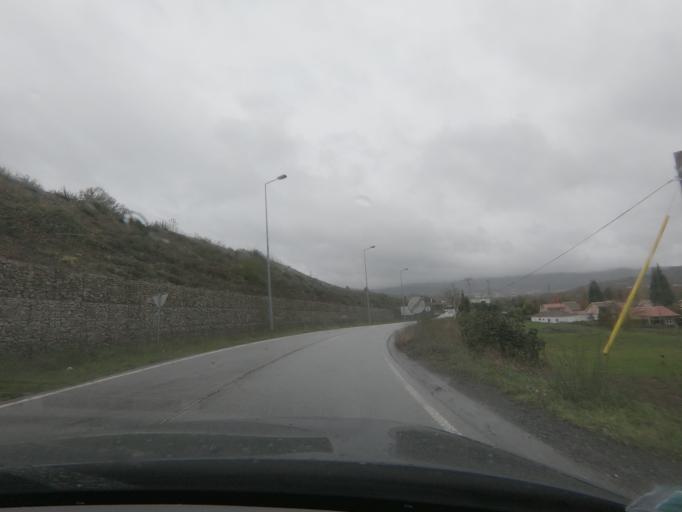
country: PT
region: Vila Real
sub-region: Santa Marta de Penaguiao
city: Santa Marta de Penaguiao
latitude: 41.2810
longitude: -7.8451
